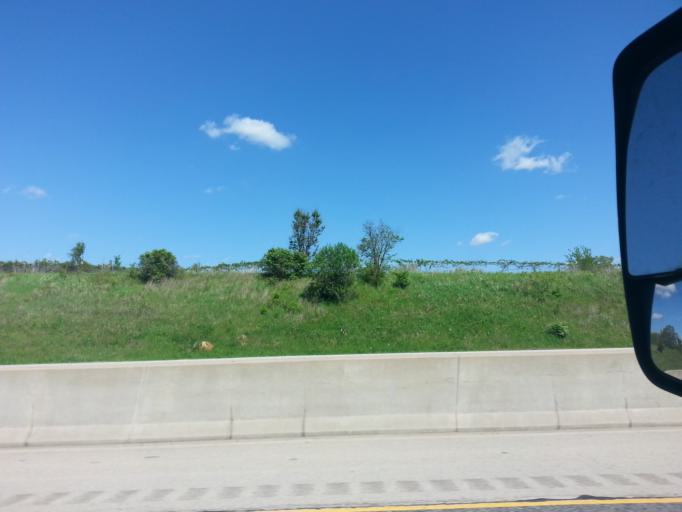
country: US
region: Illinois
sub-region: Winnebago County
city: Machesney Park
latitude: 42.3388
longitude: -88.9644
